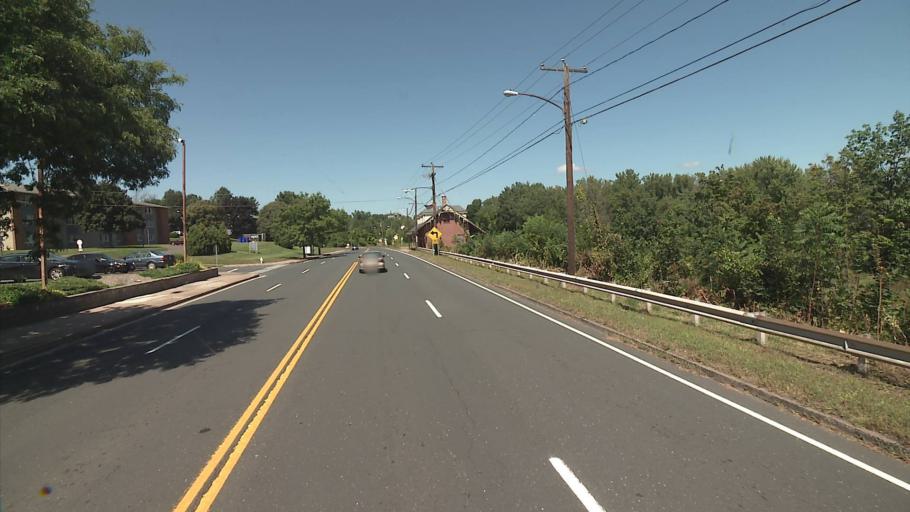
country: US
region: Connecticut
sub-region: Hartford County
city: Windsor Locks
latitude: 41.9311
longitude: -72.6276
